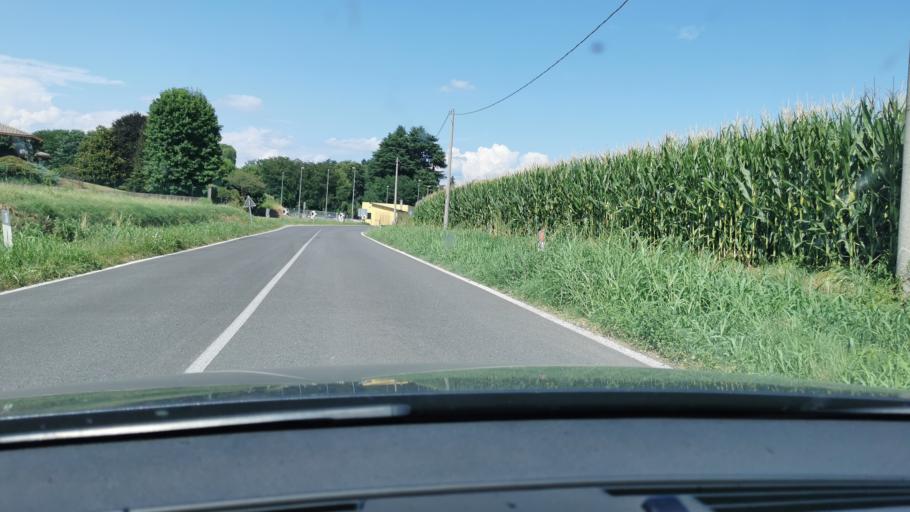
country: IT
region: Lombardy
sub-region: Provincia di Como
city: Lomazzo
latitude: 45.6917
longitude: 9.0326
